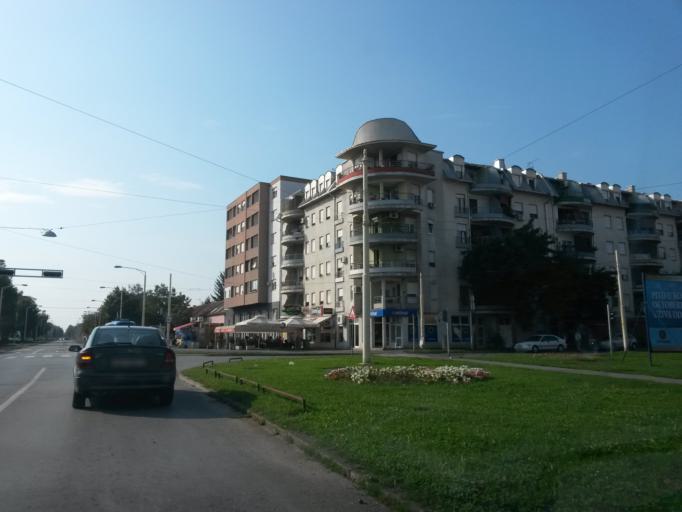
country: HR
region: Osjecko-Baranjska
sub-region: Grad Osijek
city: Osijek
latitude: 45.5523
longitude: 18.7308
